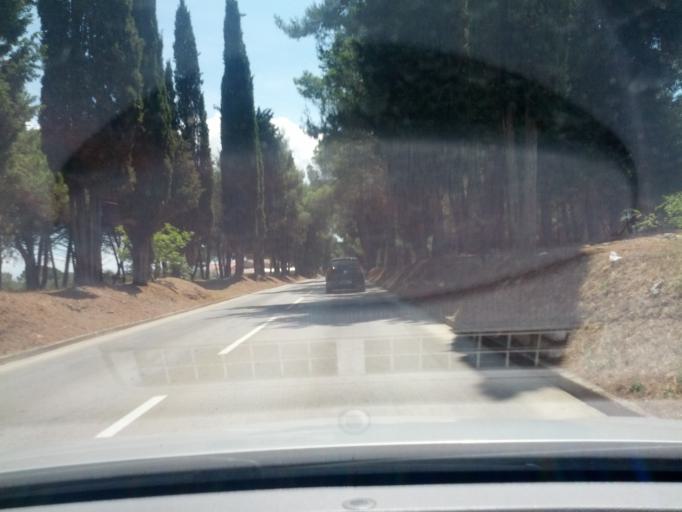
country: HR
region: Istarska
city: Fazana
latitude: 44.9186
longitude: 13.8107
